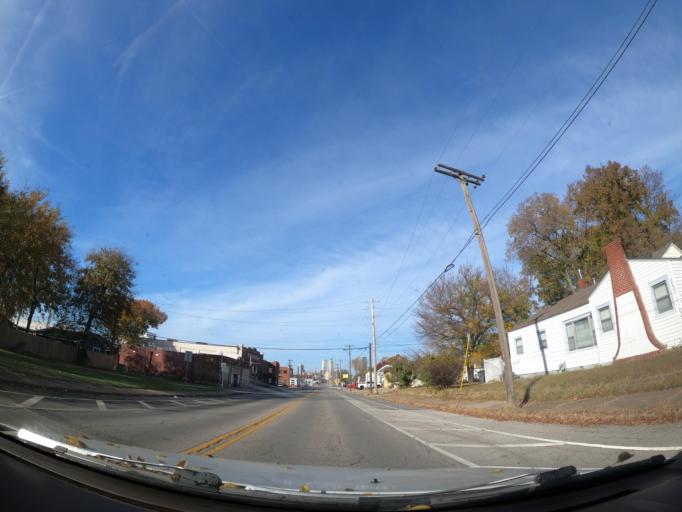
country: US
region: Oklahoma
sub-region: Tulsa County
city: Tulsa
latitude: 36.1521
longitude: -95.9623
